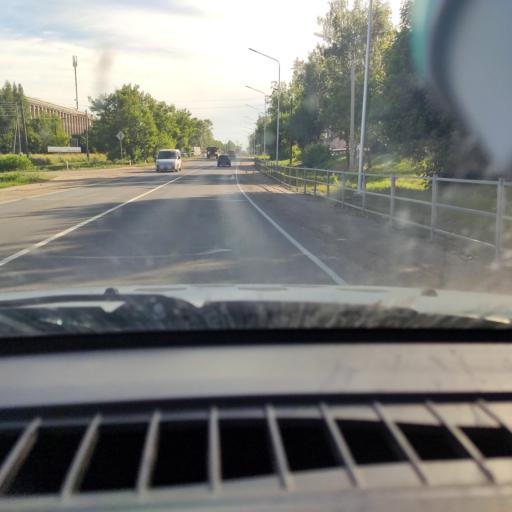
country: RU
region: Kirov
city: Vakhrushi
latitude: 58.6850
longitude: 50.0360
